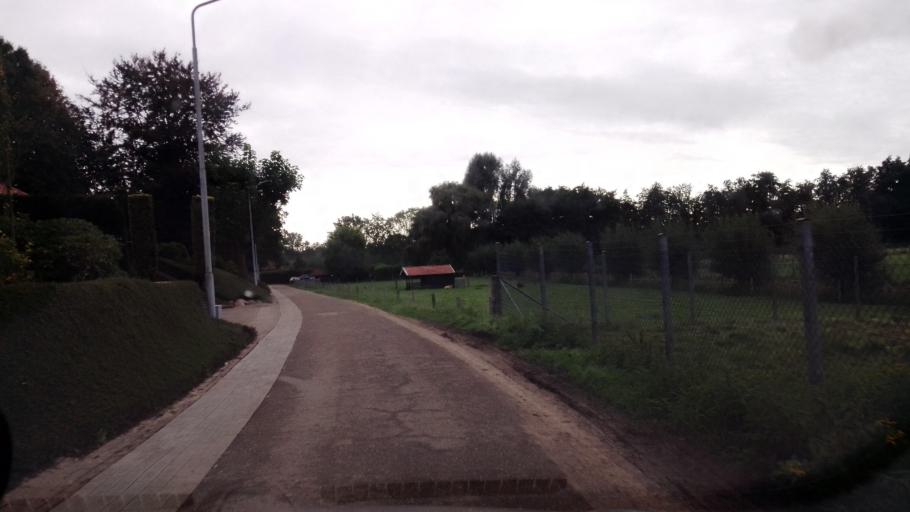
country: NL
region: Limburg
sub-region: Gemeente Venlo
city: Tegelen
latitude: 51.3539
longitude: 6.1325
